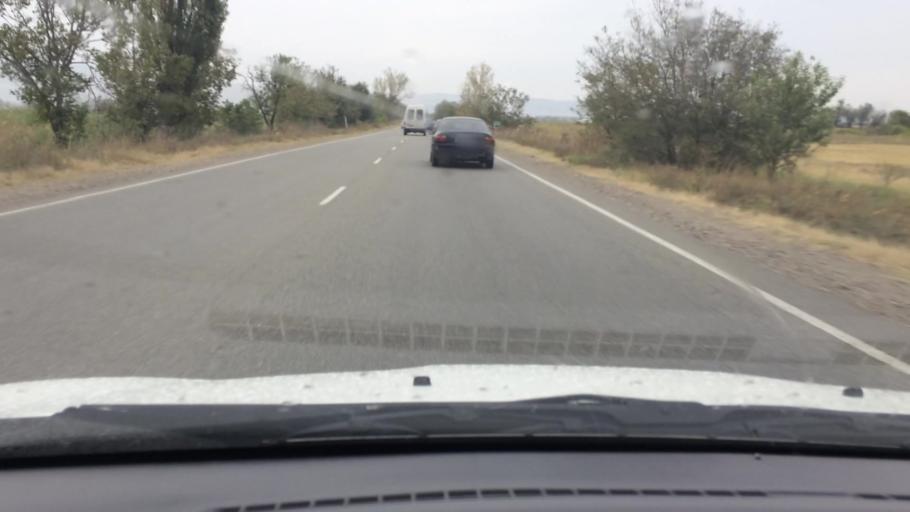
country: GE
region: Kvemo Kartli
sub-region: Marneuli
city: Marneuli
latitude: 41.5555
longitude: 44.7761
